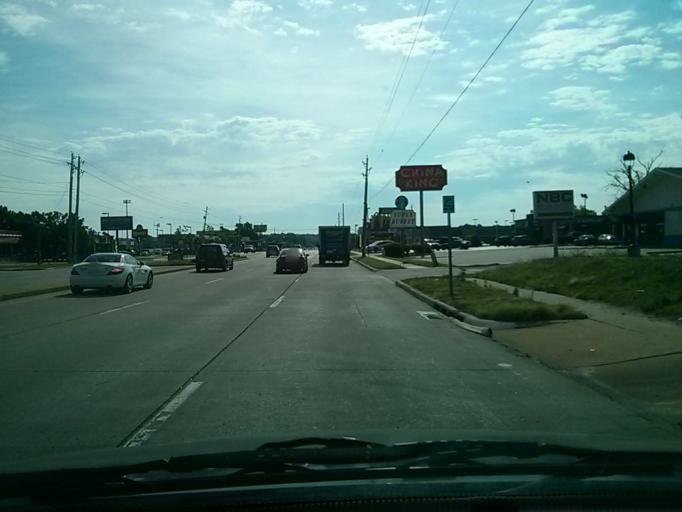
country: US
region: Oklahoma
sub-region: Tulsa County
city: Jenks
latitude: 36.0606
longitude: -95.9751
